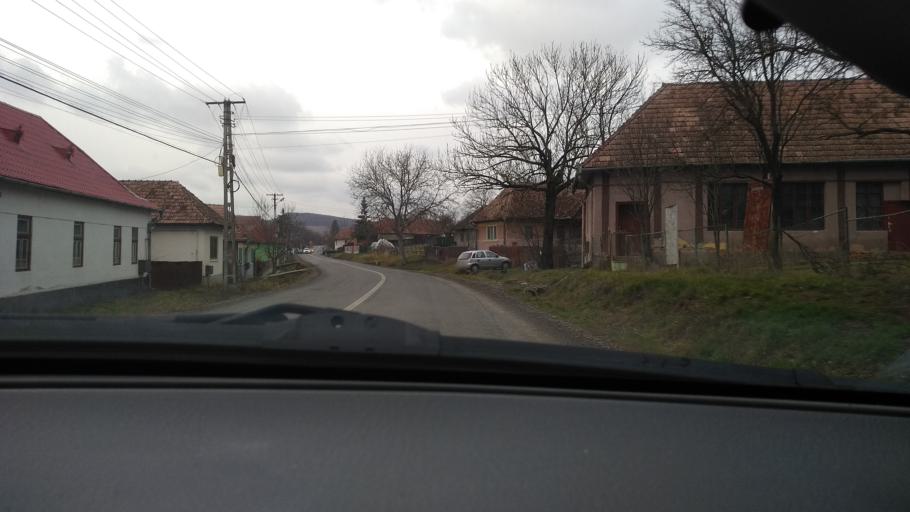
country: RO
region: Mures
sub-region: Comuna Galesti
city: Galesti
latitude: 46.5312
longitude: 24.7685
